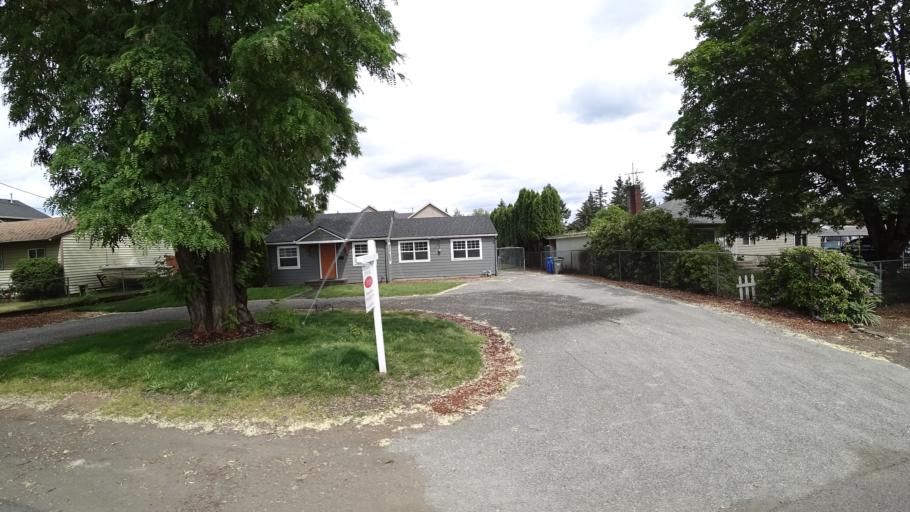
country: US
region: Oregon
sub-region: Multnomah County
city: Lents
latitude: 45.4840
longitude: -122.5492
